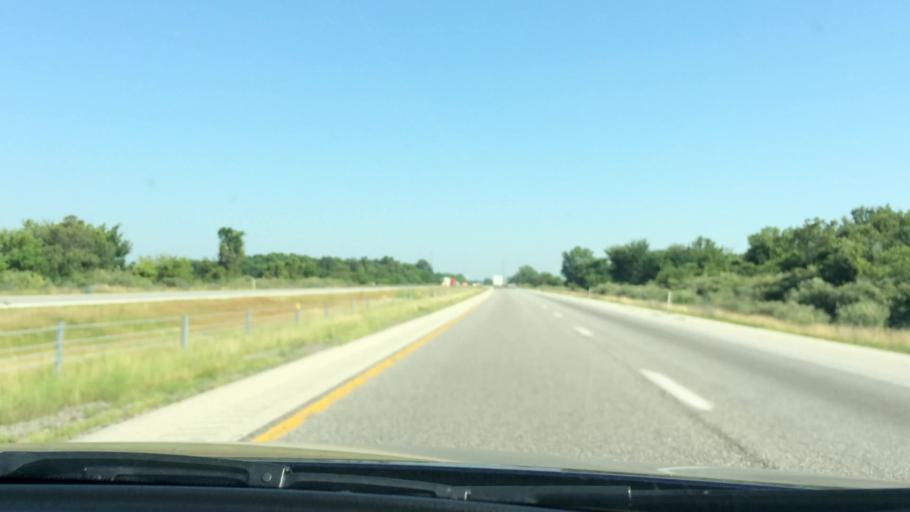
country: US
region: Indiana
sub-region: Tippecanoe County
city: Battle Ground
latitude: 40.5261
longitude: -86.9024
